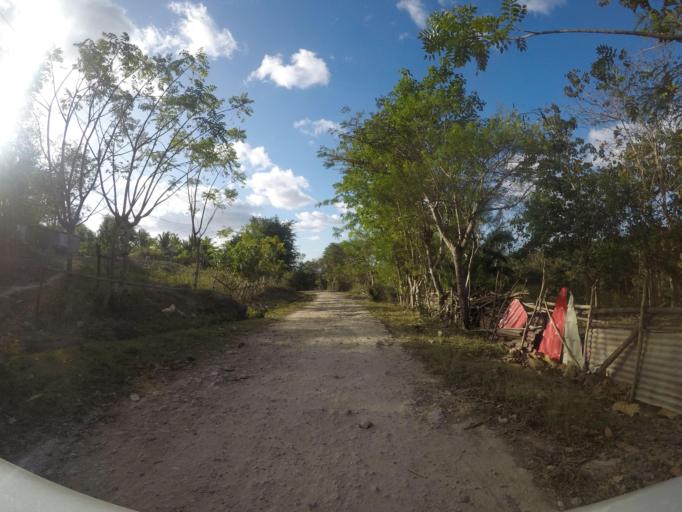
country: TL
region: Lautem
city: Lospalos
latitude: -8.4326
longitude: 126.8485
